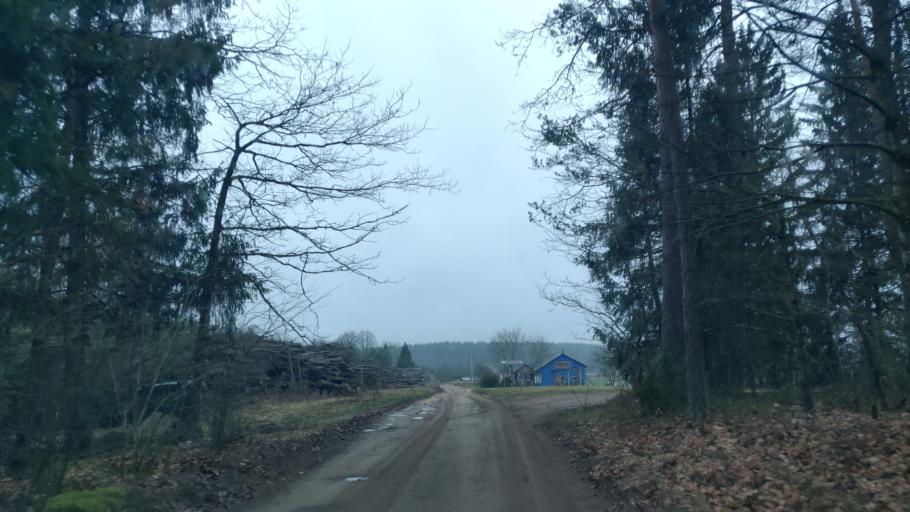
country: LT
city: Trakai
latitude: 54.5589
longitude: 24.9341
